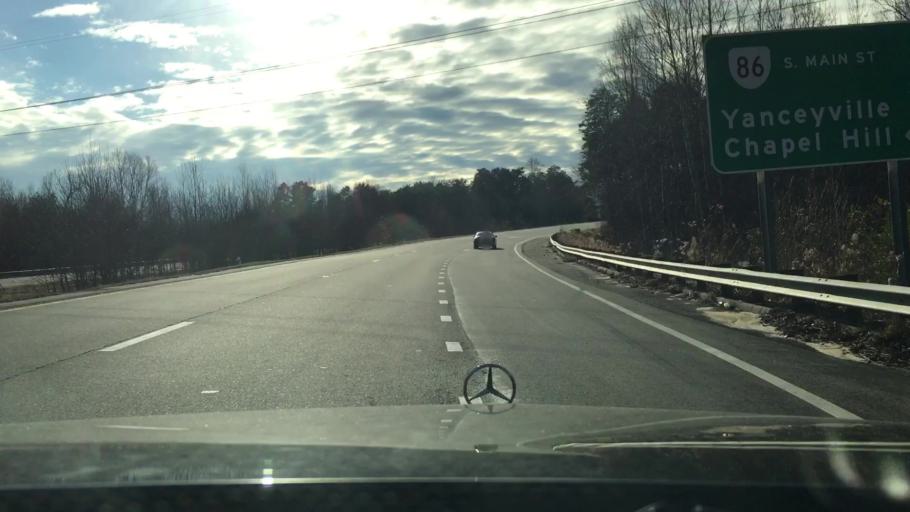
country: US
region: Virginia
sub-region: City of Danville
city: Danville
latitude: 36.5492
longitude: -79.3938
